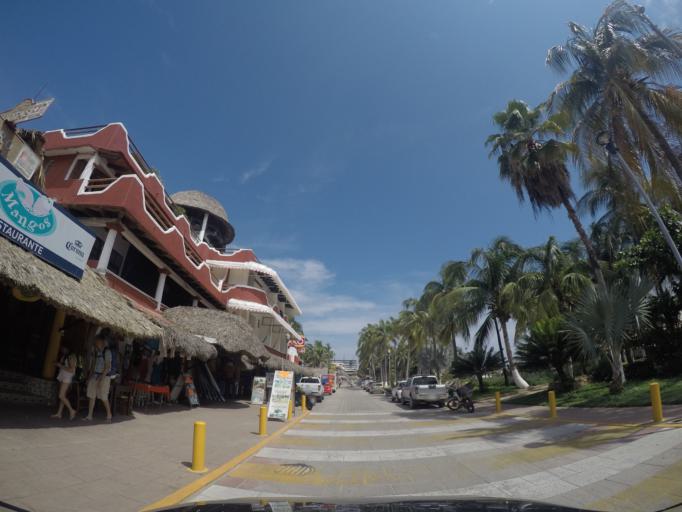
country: MX
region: Oaxaca
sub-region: Santa Maria Colotepec
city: Brisas de Zicatela
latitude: 15.8540
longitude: -97.0560
